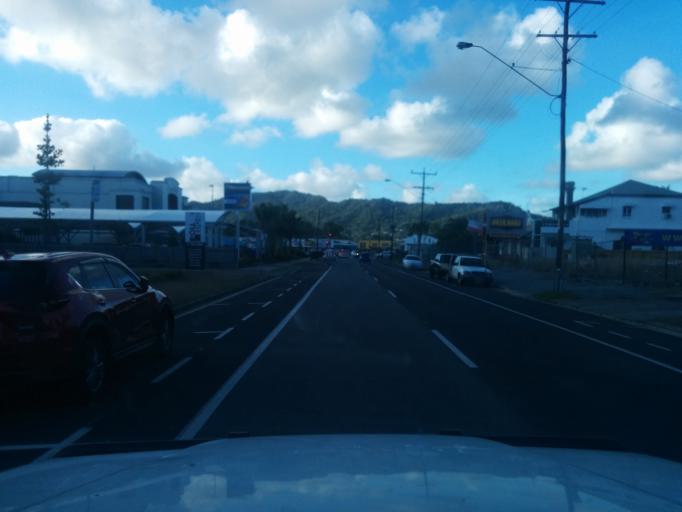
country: AU
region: Queensland
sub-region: Cairns
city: Cairns
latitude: -16.9171
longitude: 145.7472
